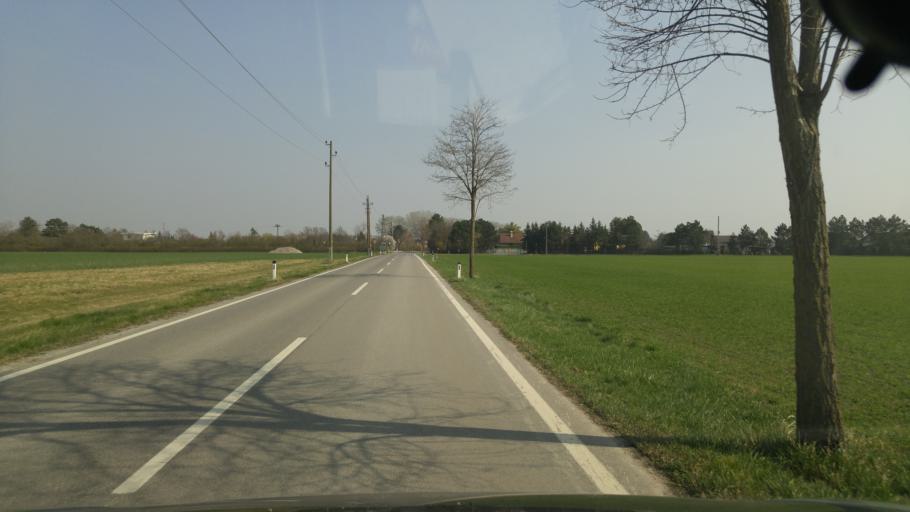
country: AT
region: Lower Austria
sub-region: Politischer Bezirk Modling
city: Munchendorf
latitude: 48.0335
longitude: 16.4066
